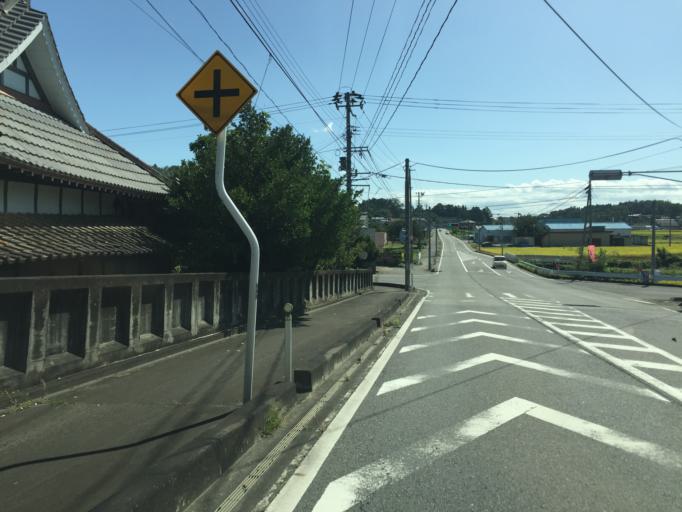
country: JP
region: Fukushima
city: Sukagawa
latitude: 37.2744
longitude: 140.4200
